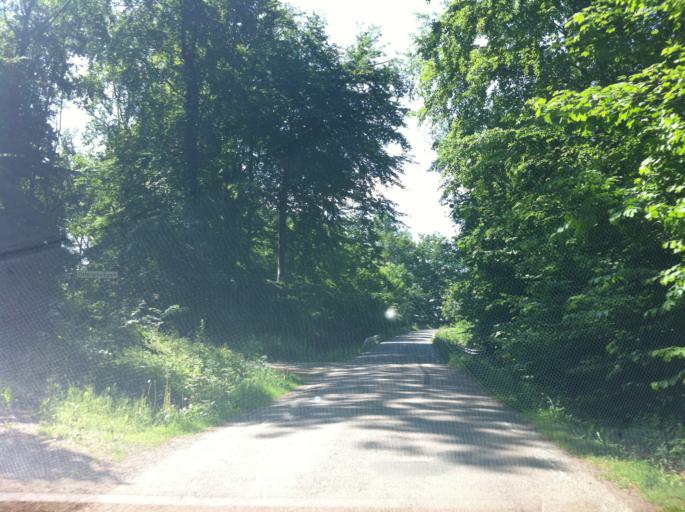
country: SE
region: Skane
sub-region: Landskrona
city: Asmundtorp
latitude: 55.9429
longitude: 12.9166
